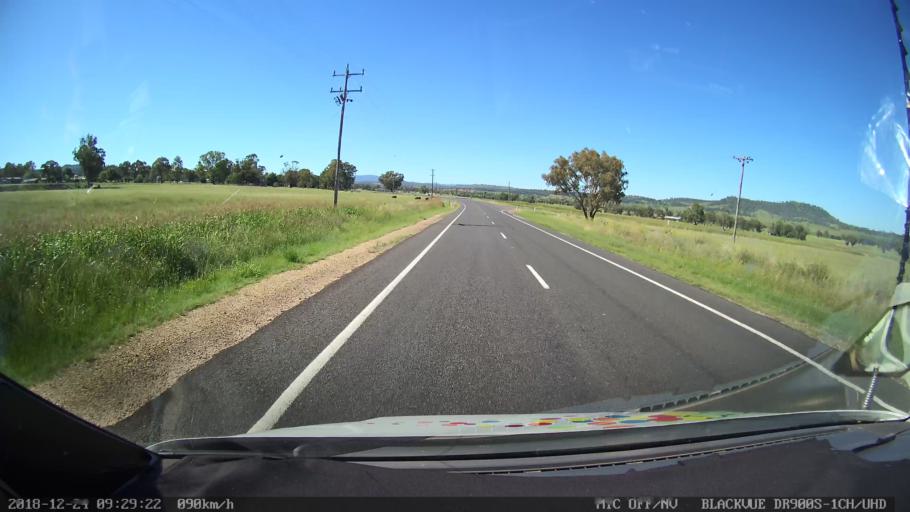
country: AU
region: New South Wales
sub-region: Liverpool Plains
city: Quirindi
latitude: -31.5496
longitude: 150.6922
